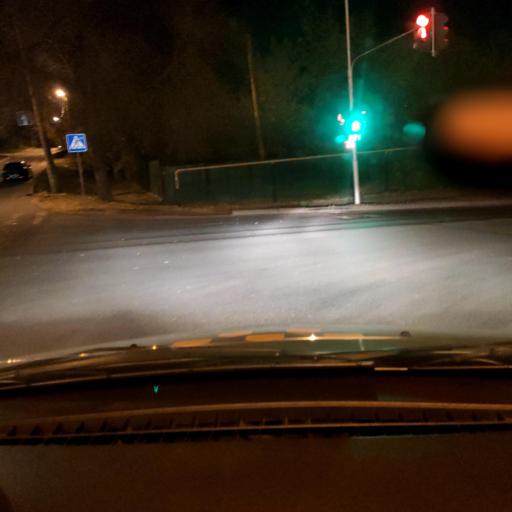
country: RU
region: Bashkortostan
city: Ufa
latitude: 54.7442
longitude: 55.9512
